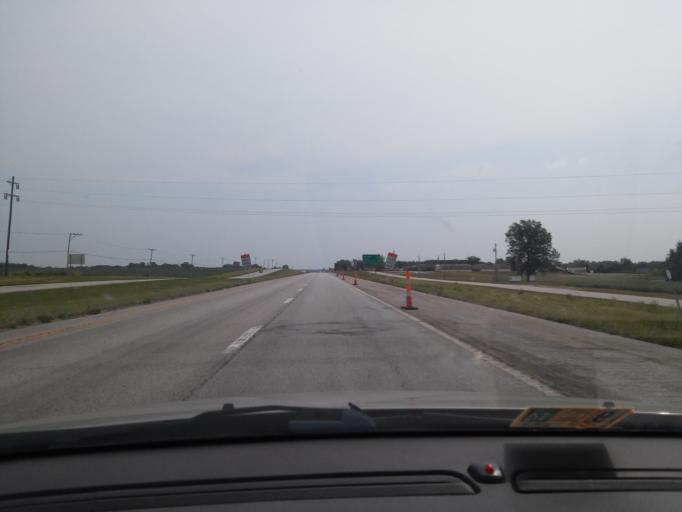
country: US
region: Missouri
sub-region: Callaway County
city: Fulton
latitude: 38.9602
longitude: -91.9246
